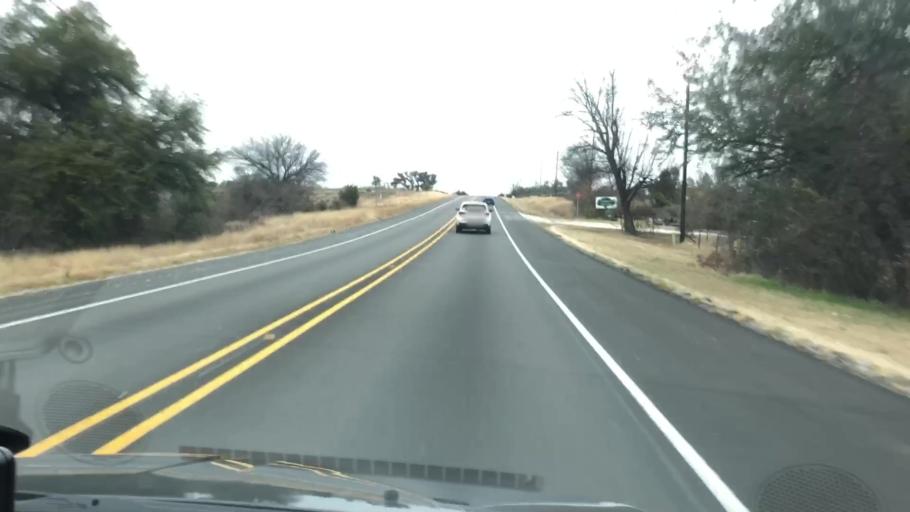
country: US
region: Texas
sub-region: Erath County
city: Stephenville
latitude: 32.3156
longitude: -98.1830
